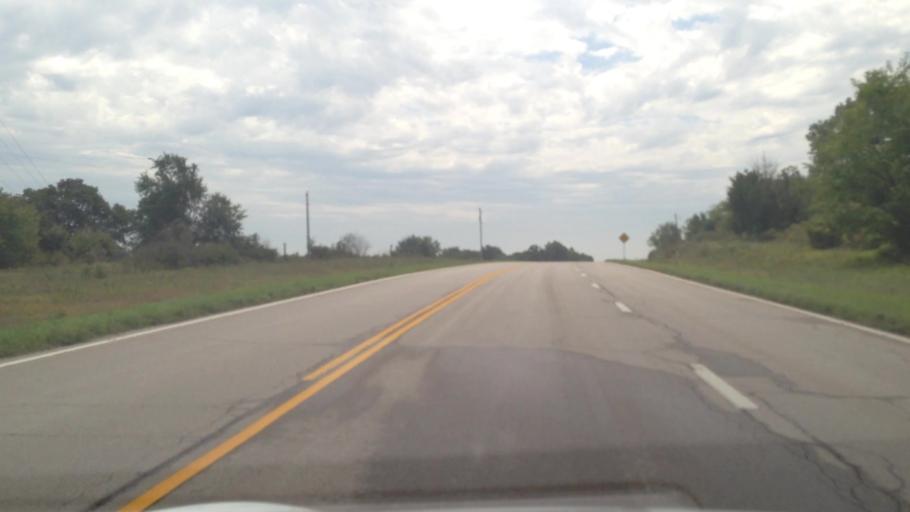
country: US
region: Kansas
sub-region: Bourbon County
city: Fort Scott
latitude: 37.8278
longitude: -94.9794
